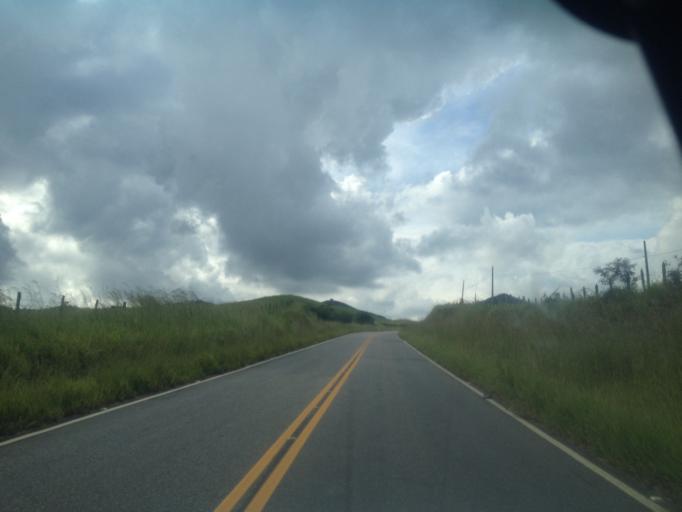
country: BR
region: Rio de Janeiro
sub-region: Quatis
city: Quatis
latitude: -22.3972
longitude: -44.2657
